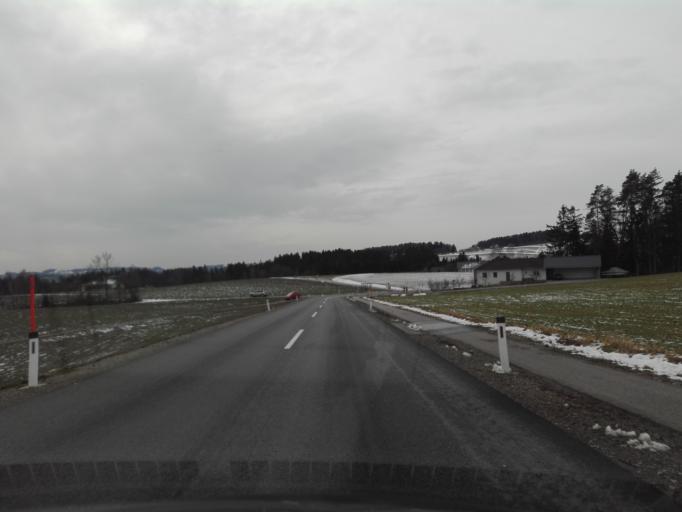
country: AT
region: Upper Austria
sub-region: Politischer Bezirk Rohrbach
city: Kleinzell im Muehlkreis
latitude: 48.4567
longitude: 14.0224
